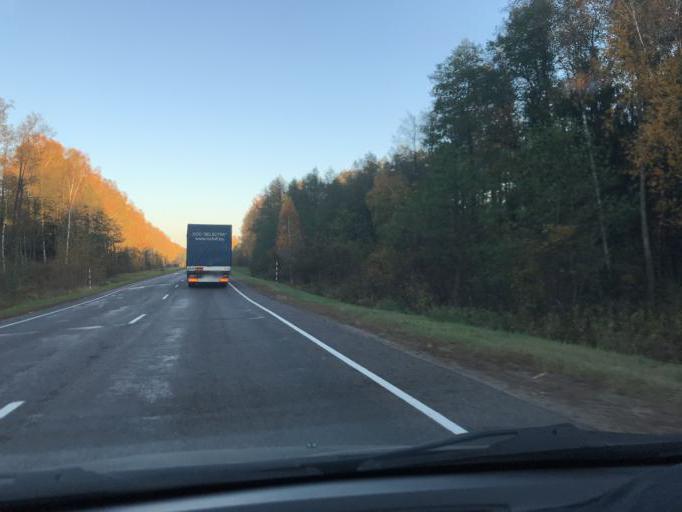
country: BY
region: Minsk
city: Staryya Darohi
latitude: 53.0388
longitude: 28.1917
